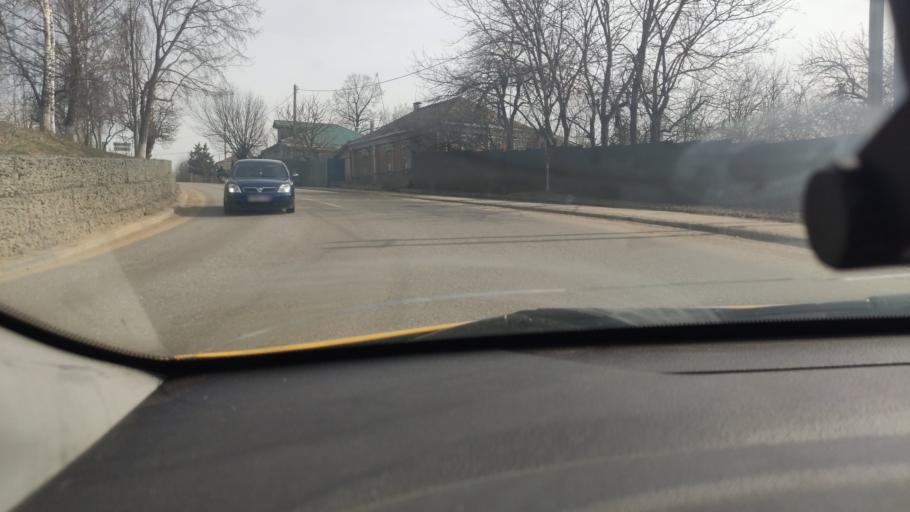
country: RU
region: Moskovskaya
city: Ruza
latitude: 55.6955
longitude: 36.1994
